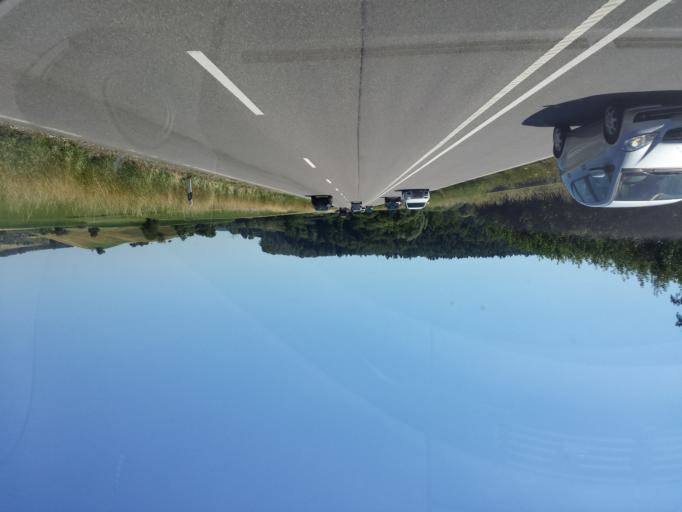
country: DE
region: Baden-Wuerttemberg
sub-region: Tuebingen Region
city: Sipplingen
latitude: 47.8024
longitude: 9.1298
